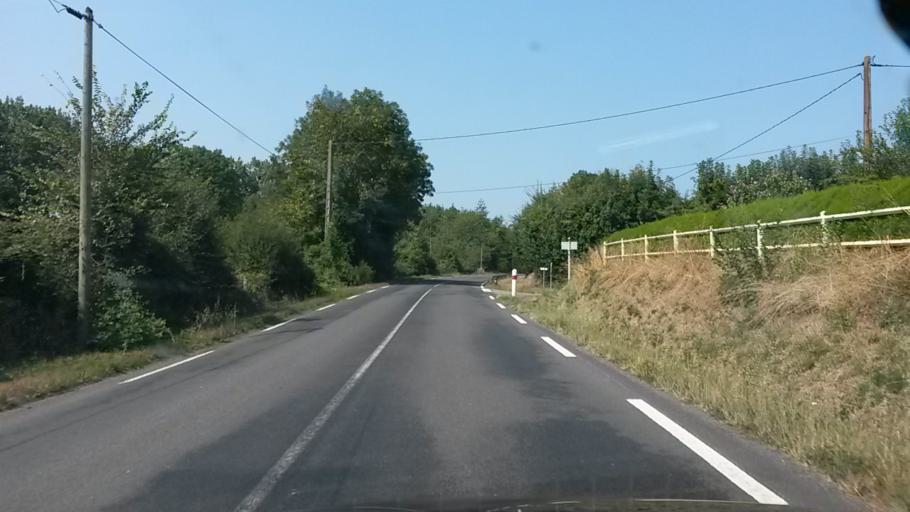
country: FR
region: Lower Normandy
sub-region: Departement de l'Orne
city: Conde-sur-Sarthe
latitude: 48.4181
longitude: -0.0058
